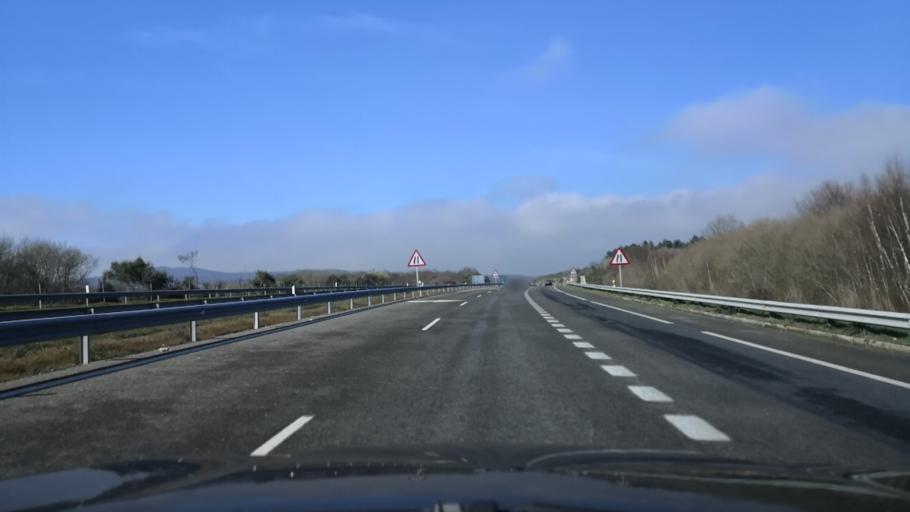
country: ES
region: Galicia
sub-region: Provincia de Ourense
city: Taboadela
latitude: 42.2104
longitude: -7.8336
